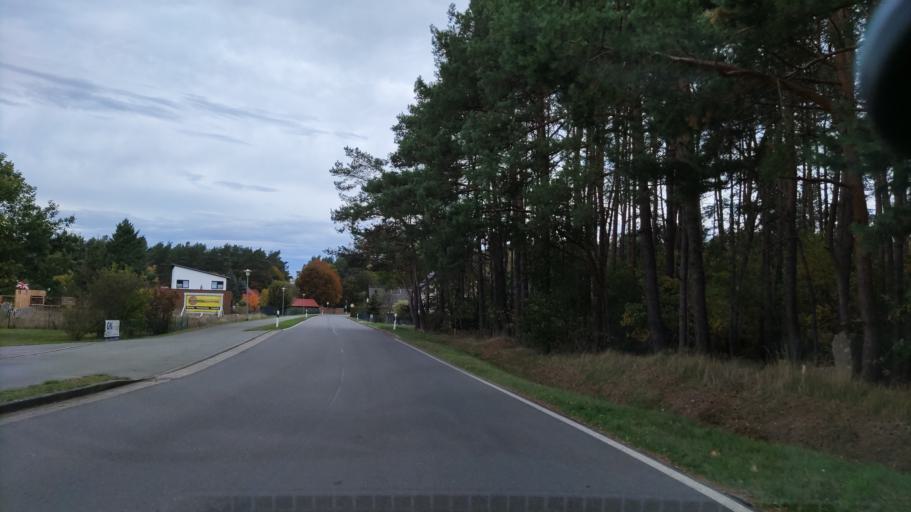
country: DE
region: Mecklenburg-Vorpommern
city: Boizenburg
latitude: 53.3774
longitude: 10.8574
